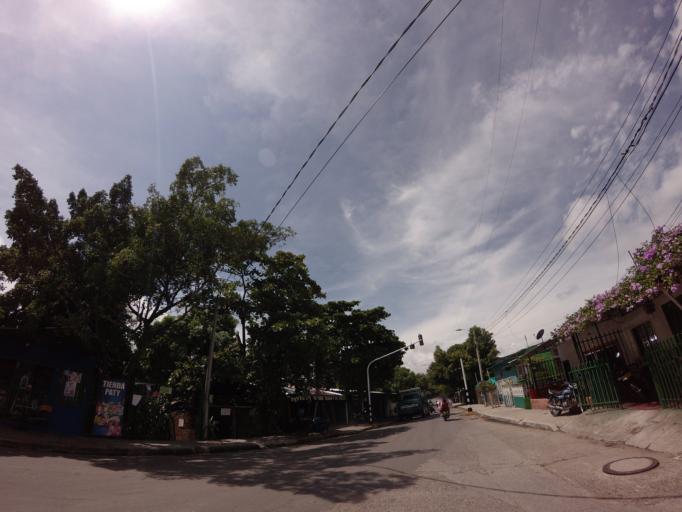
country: CO
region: Cundinamarca
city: Puerto Salgar
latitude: 5.4719
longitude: -74.6692
